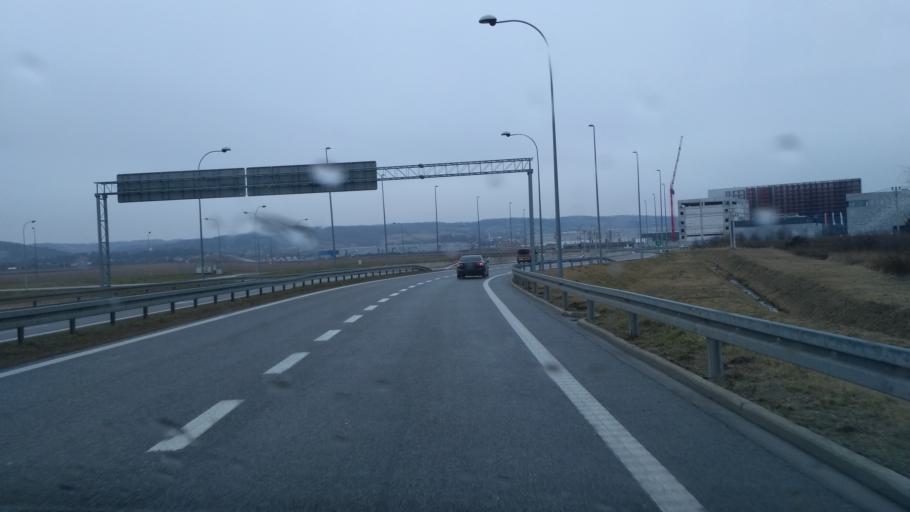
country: PL
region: Subcarpathian Voivodeship
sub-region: Powiat debicki
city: Brzeznica
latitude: 50.0782
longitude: 21.4701
